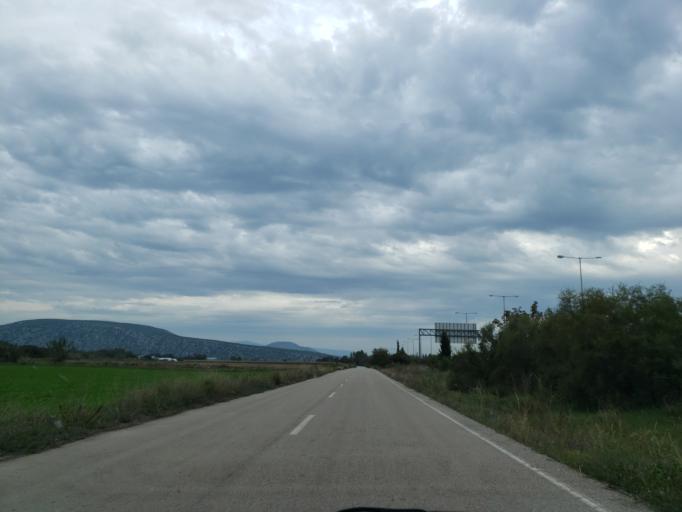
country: GR
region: Central Greece
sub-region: Nomos Voiotias
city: Akraifnia
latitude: 38.4847
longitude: 23.1643
